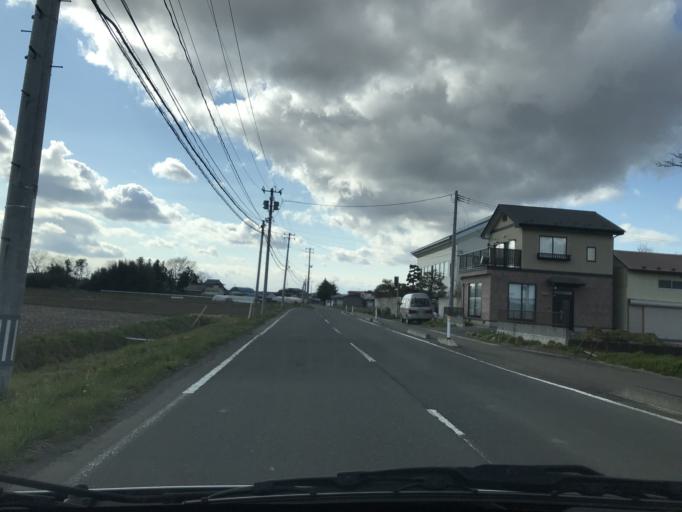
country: JP
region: Miyagi
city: Wakuya
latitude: 38.6649
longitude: 141.1808
